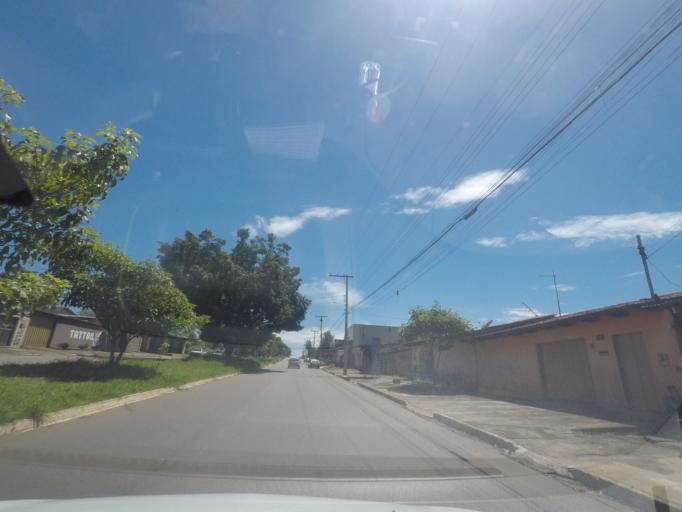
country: BR
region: Goias
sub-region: Aparecida De Goiania
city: Aparecida de Goiania
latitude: -16.7732
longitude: -49.3253
